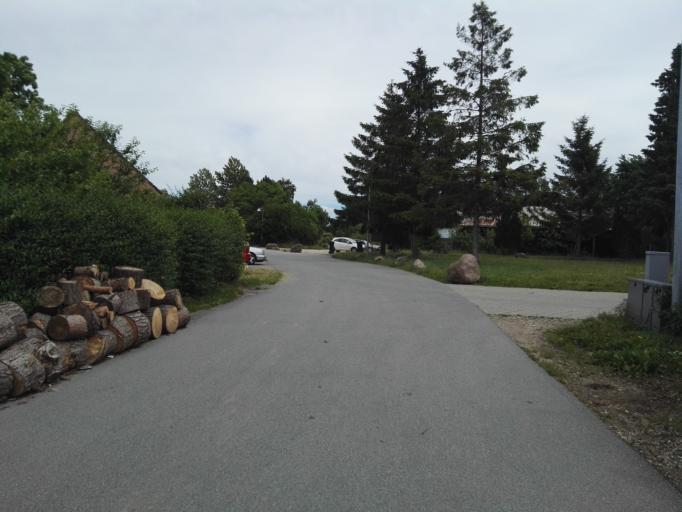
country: DK
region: Capital Region
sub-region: Hillerod Kommune
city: Skaevinge
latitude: 55.9107
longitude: 12.1495
